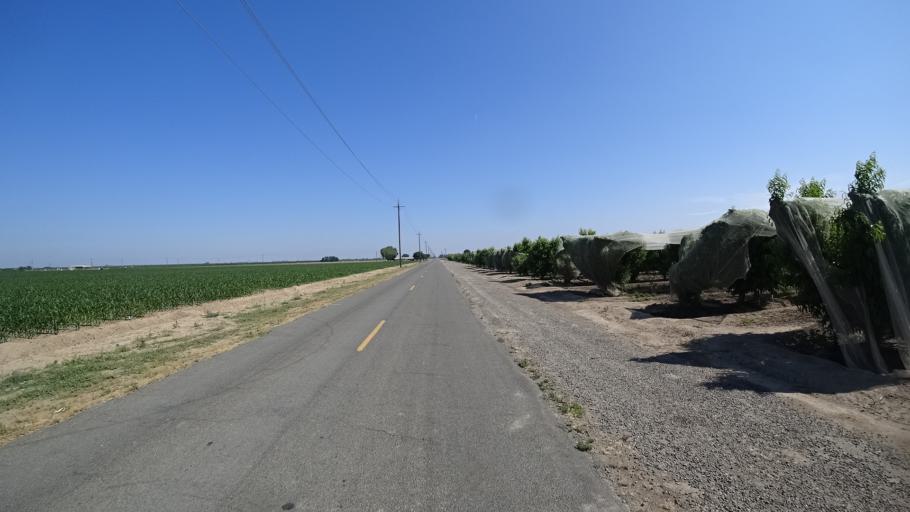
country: US
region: California
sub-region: Kings County
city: Lucerne
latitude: 36.3981
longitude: -119.5829
